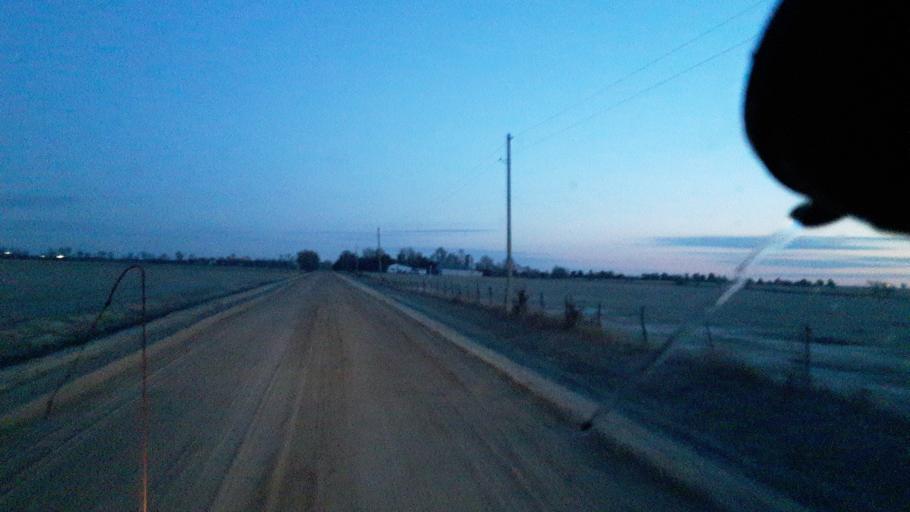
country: US
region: Kansas
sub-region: Reno County
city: South Hutchinson
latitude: 37.9856
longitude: -97.9773
